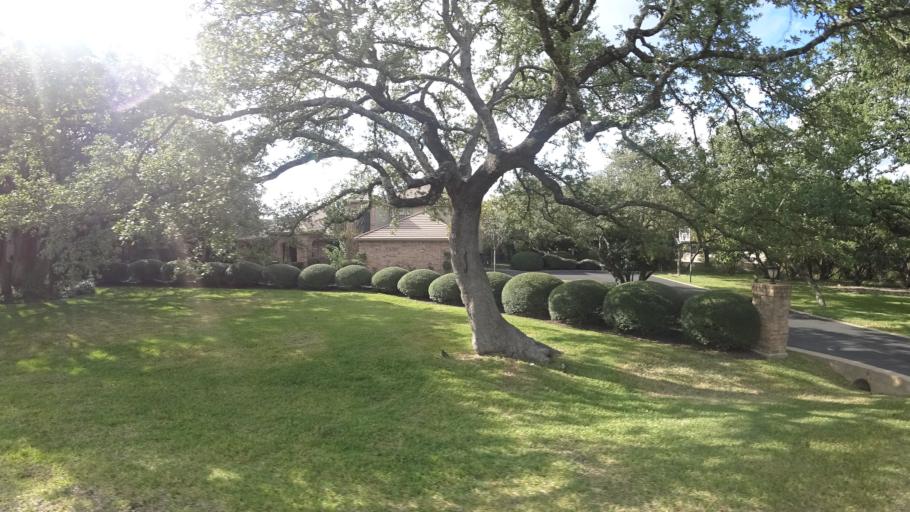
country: US
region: Texas
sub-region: Travis County
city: Barton Creek
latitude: 30.2833
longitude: -97.8814
